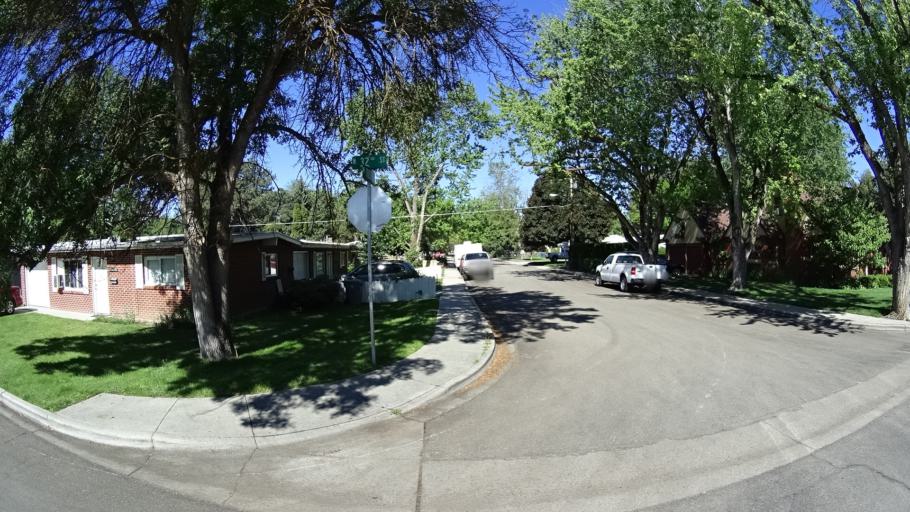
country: US
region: Idaho
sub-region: Ada County
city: Garden City
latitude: 43.6495
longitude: -116.2284
